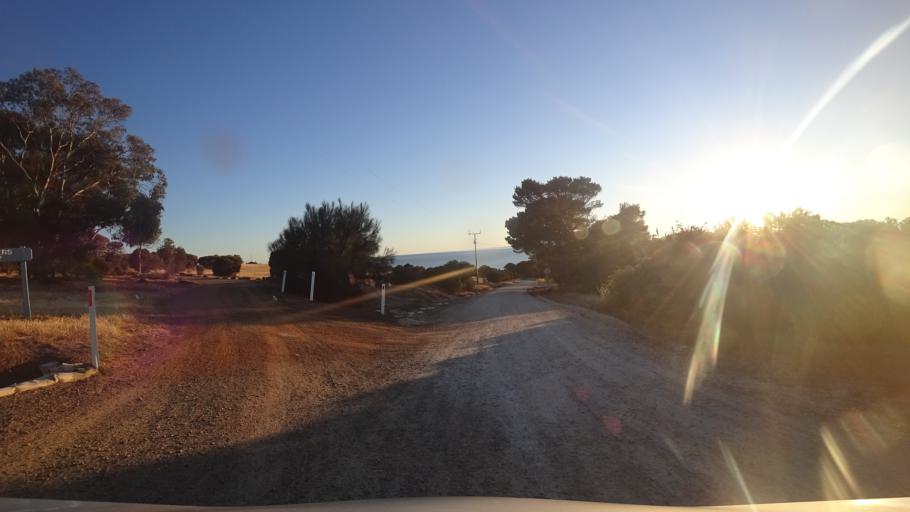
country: AU
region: South Australia
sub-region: Kangaroo Island
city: Kingscote
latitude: -35.6455
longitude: 137.6354
